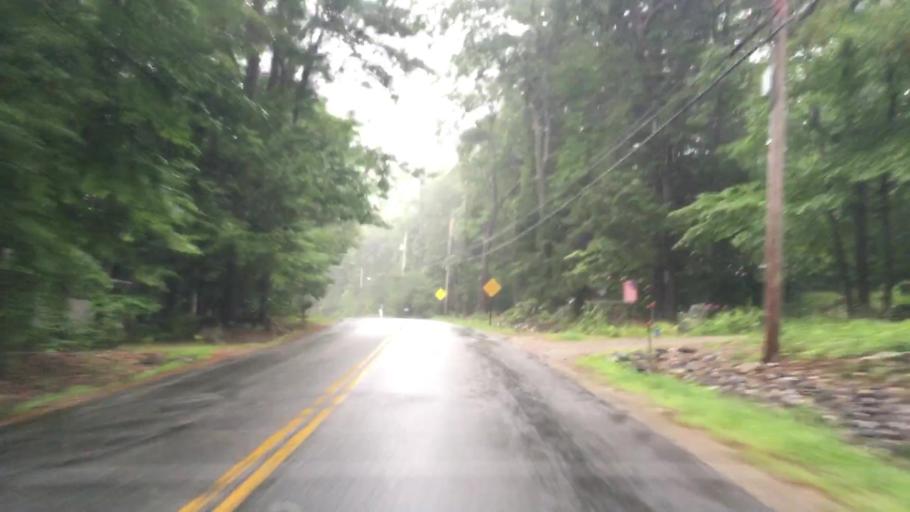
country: US
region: Maine
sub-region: Oxford County
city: Lovell
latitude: 44.0711
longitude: -70.8205
